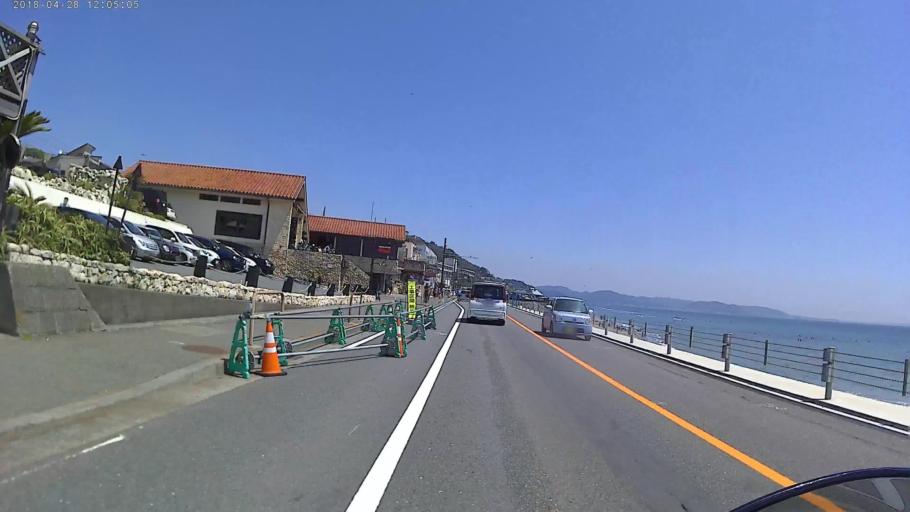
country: JP
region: Kanagawa
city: Kamakura
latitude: 35.3056
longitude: 139.5083
